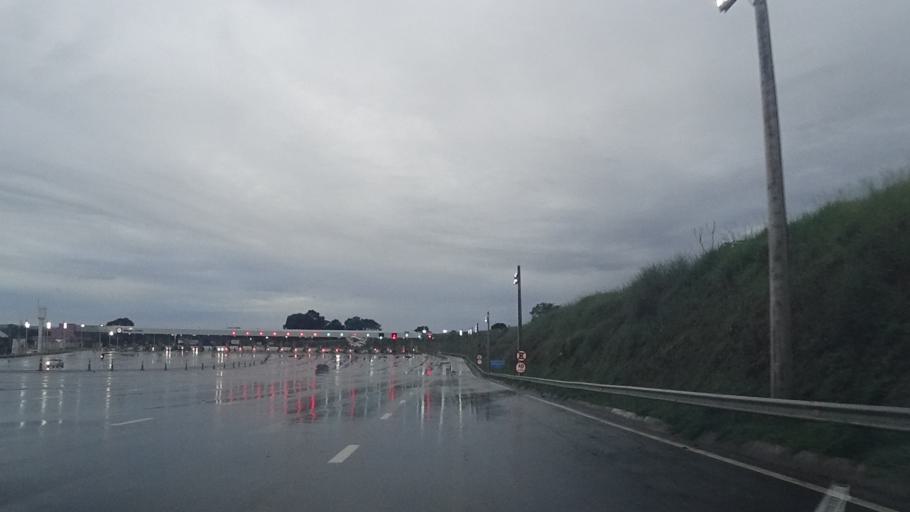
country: BR
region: Goias
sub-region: Goianapolis
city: Goianapolis
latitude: -16.4356
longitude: -49.0191
